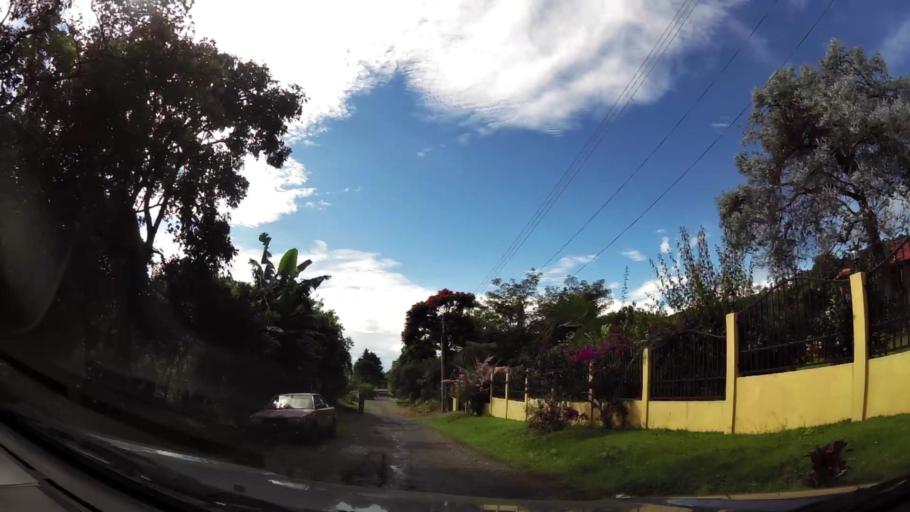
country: PA
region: Chiriqui
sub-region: Distrito Boquete
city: Boquete
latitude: 8.7794
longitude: -82.4347
